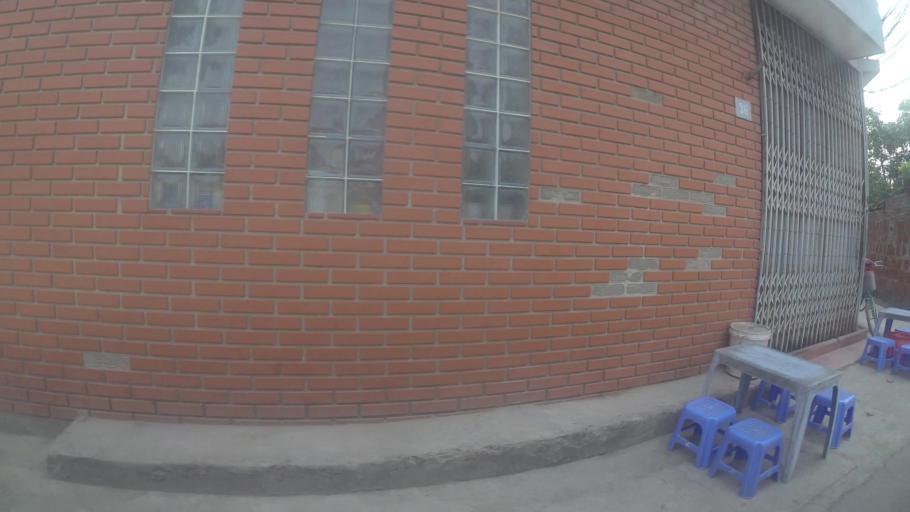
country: VN
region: Ha Noi
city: Ha Dong
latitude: 20.9947
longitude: 105.7557
